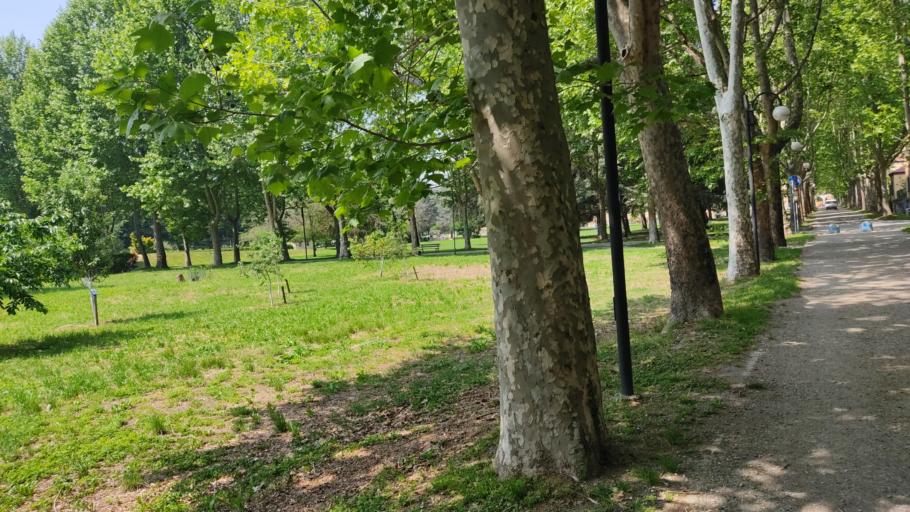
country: IT
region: Piedmont
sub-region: Provincia di Torino
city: Collegno
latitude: 45.0817
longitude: 7.5796
